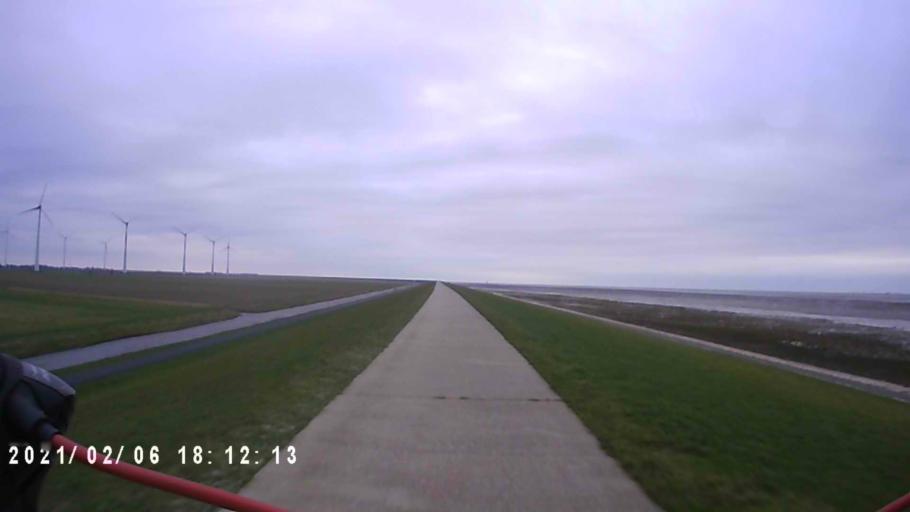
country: DE
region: Lower Saxony
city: Borkum
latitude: 53.4606
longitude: 6.7774
